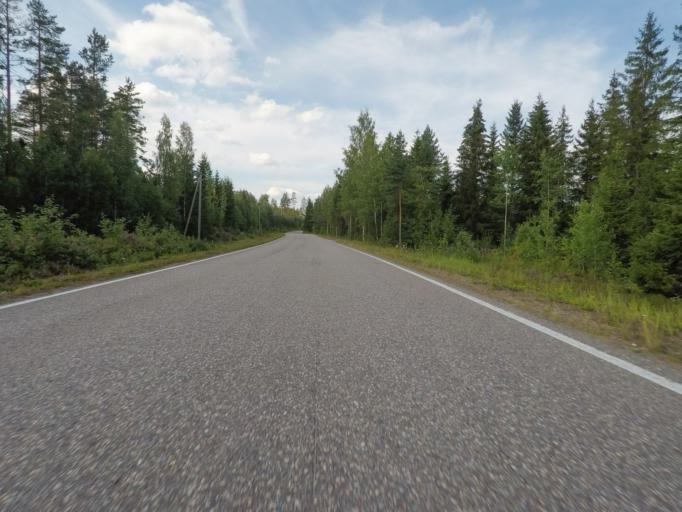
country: FI
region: Southern Savonia
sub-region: Savonlinna
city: Sulkava
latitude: 61.7441
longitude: 28.1994
